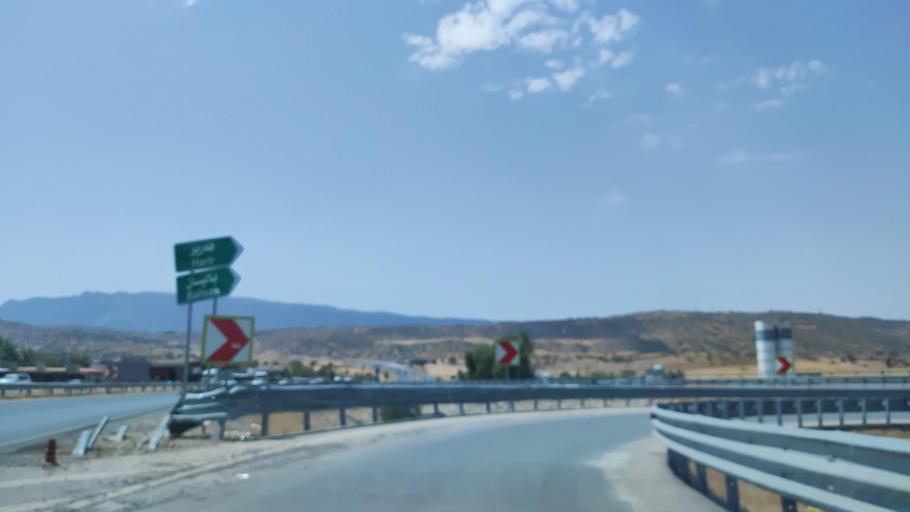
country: IQ
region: Arbil
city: Shaqlawah
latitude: 36.4566
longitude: 44.3838
